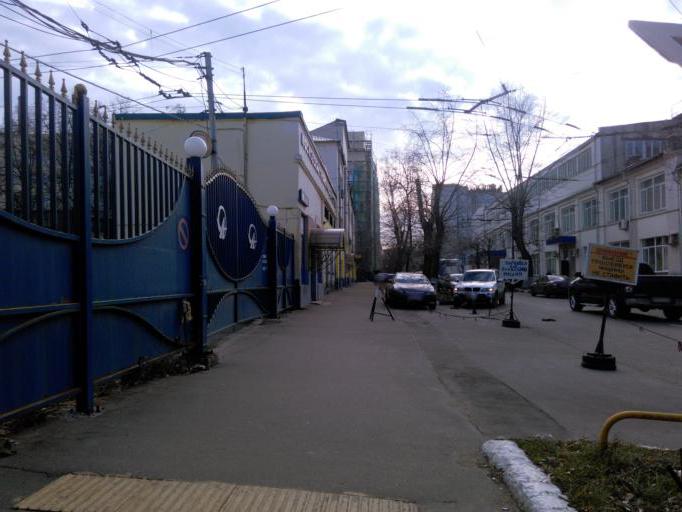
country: RU
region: Moscow
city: Mar'ina Roshcha
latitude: 55.8023
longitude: 37.5850
